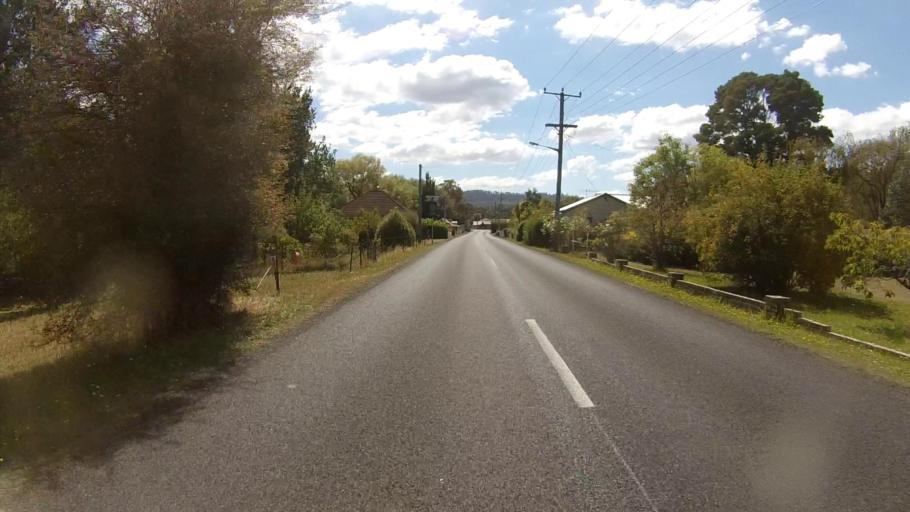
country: AU
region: Tasmania
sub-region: Derwent Valley
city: New Norfolk
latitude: -42.6805
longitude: 146.7852
